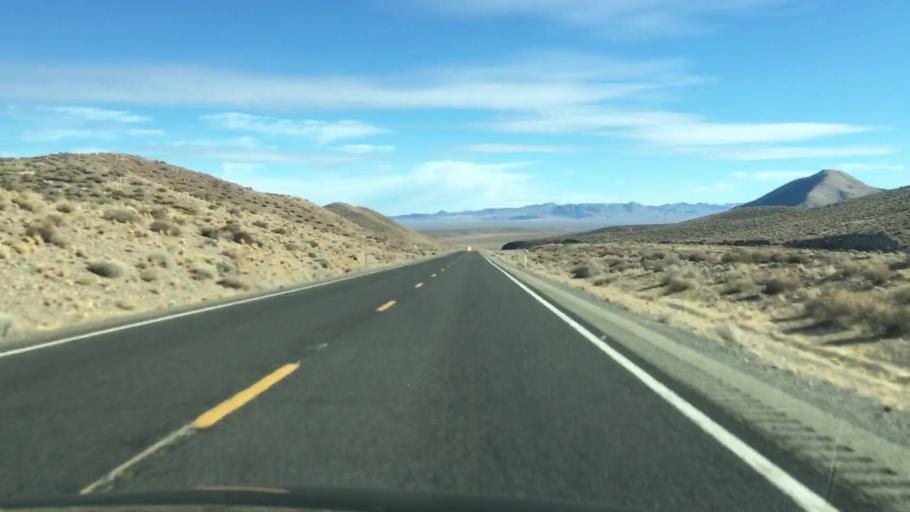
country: US
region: Nevada
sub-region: Lyon County
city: Yerington
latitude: 39.0399
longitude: -118.9379
